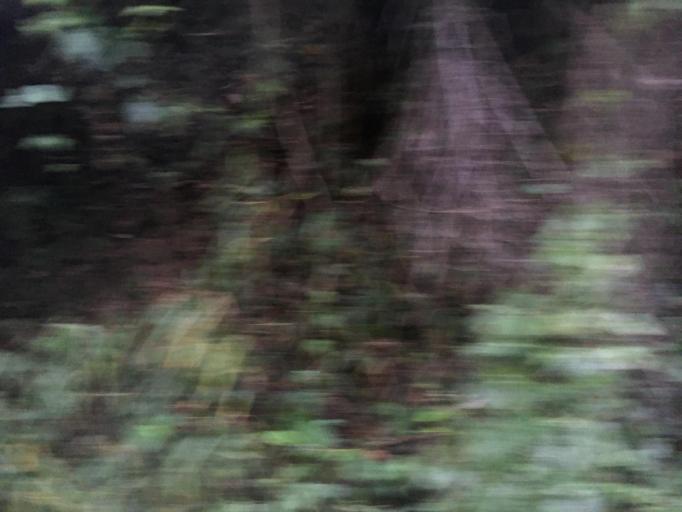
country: TW
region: Taiwan
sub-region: Chiayi
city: Jiayi Shi
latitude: 23.5468
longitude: 120.6098
